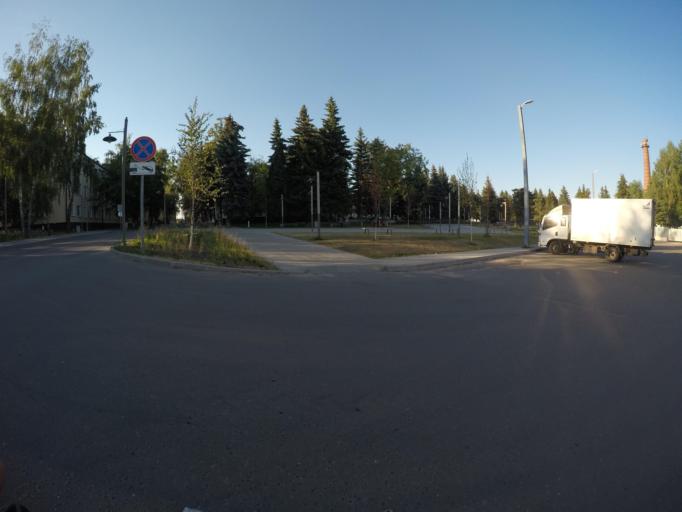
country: RU
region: Moskovskaya
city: Rechitsy
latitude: 55.5854
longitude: 38.5043
